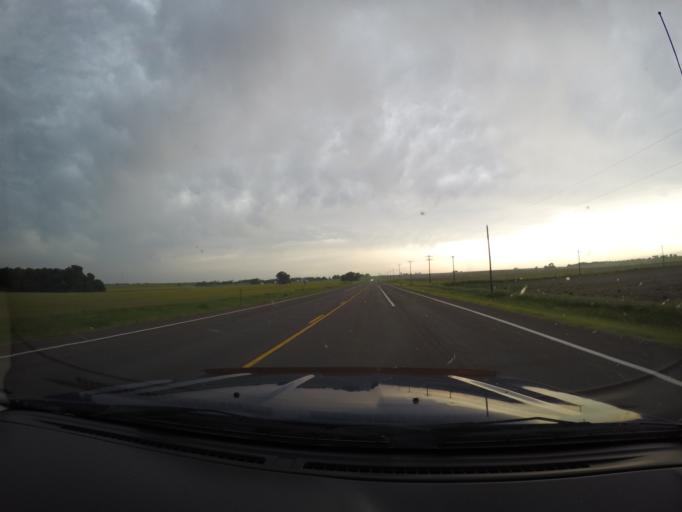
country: US
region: Kansas
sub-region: Clay County
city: Clay Center
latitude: 39.3810
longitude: -97.0718
